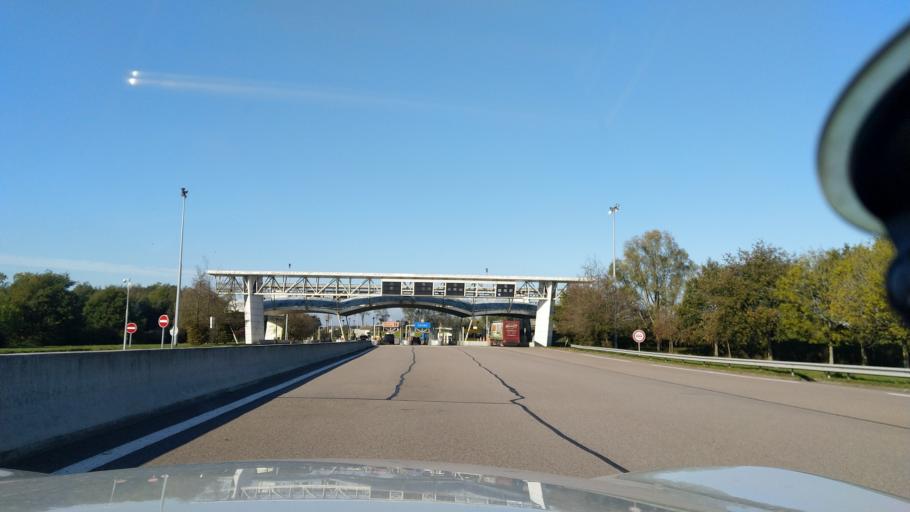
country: FR
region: Haute-Normandie
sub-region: Departement de la Seine-Maritime
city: Valliquerville
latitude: 49.6323
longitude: 0.6418
